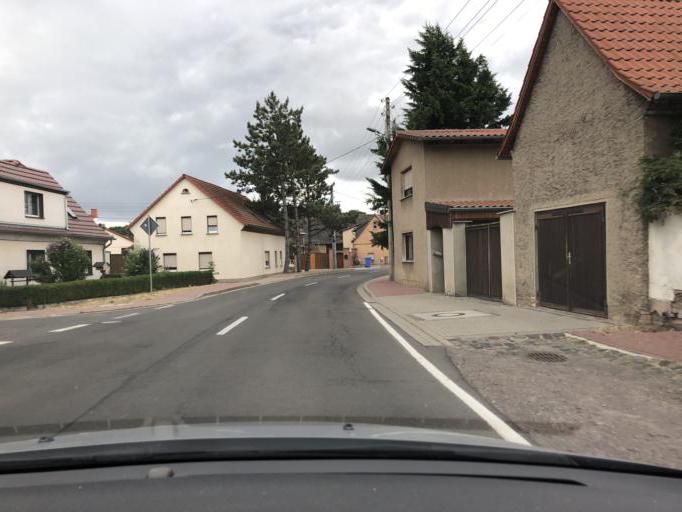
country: DE
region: Saxony-Anhalt
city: Ermlitz
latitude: 51.3872
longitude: 12.1433
